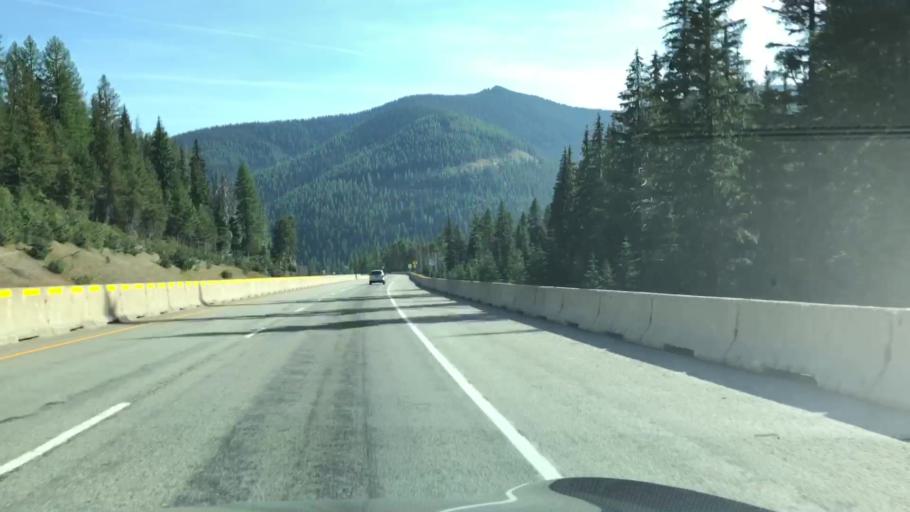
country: US
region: Idaho
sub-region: Shoshone County
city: Wallace
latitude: 47.4512
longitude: -115.6939
